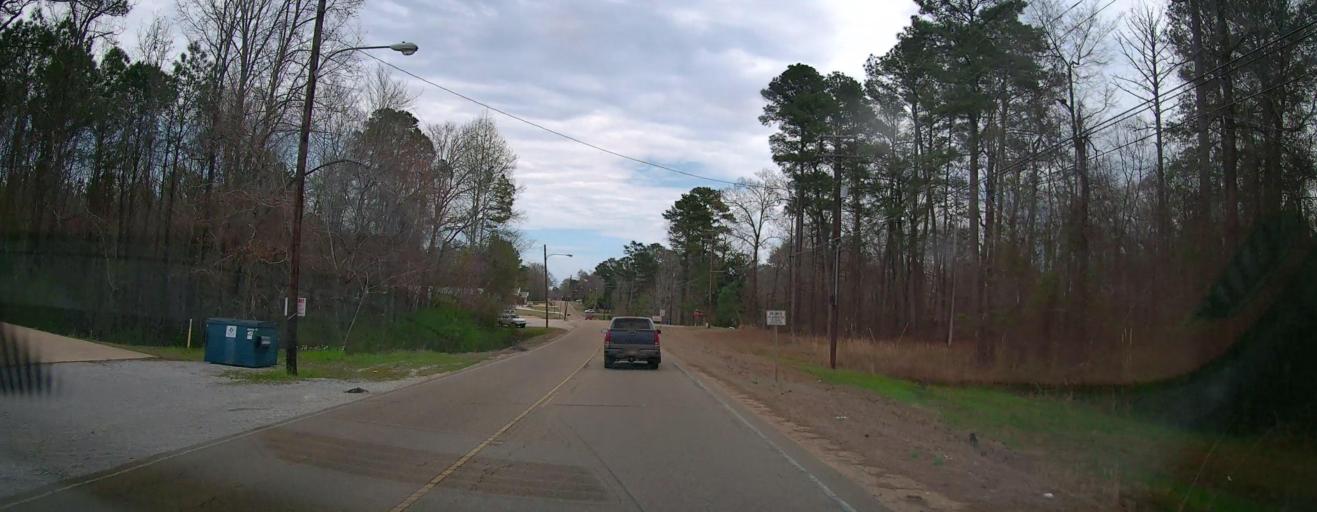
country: US
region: Mississippi
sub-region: Itawamba County
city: Fulton
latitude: 34.2729
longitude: -88.3907
